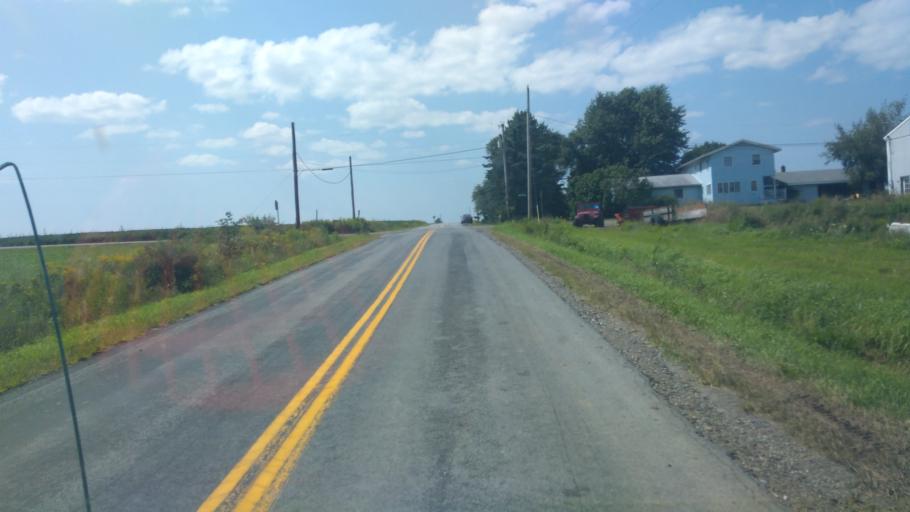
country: US
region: New York
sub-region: Steuben County
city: Canisteo
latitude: 42.3506
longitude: -77.5768
